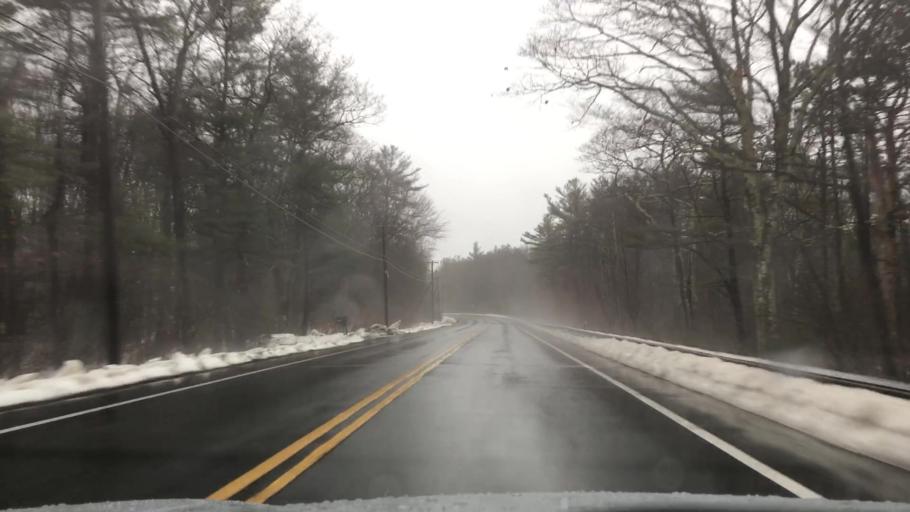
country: US
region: Massachusetts
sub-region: Hampshire County
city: Pelham
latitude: 42.3795
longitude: -72.4010
